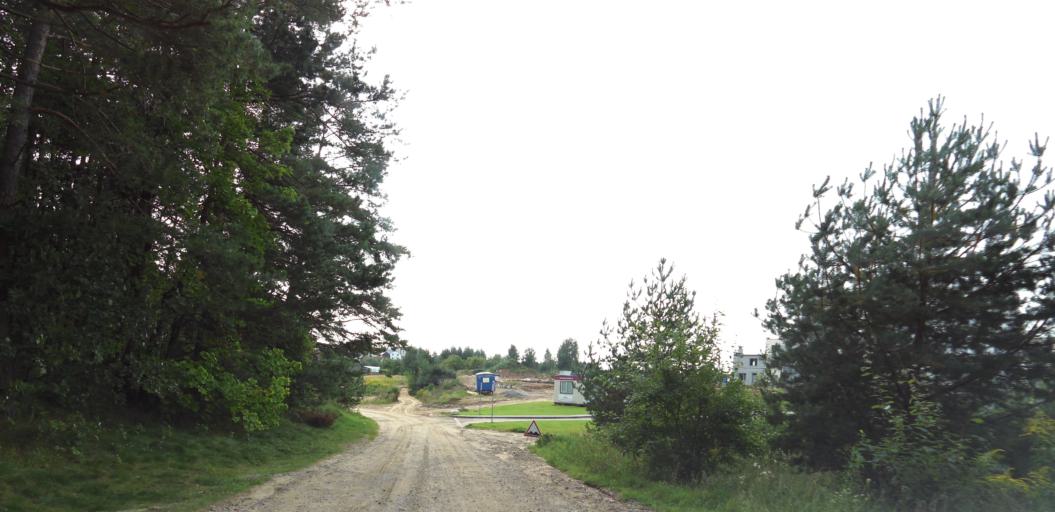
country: LT
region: Vilnius County
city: Pasilaiciai
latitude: 54.7523
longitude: 25.2290
